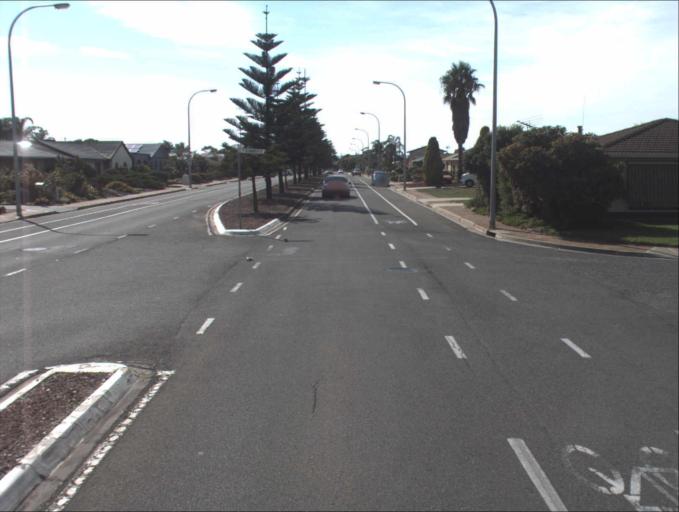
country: AU
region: South Australia
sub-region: Port Adelaide Enfield
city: Birkenhead
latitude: -34.7925
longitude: 138.4930
